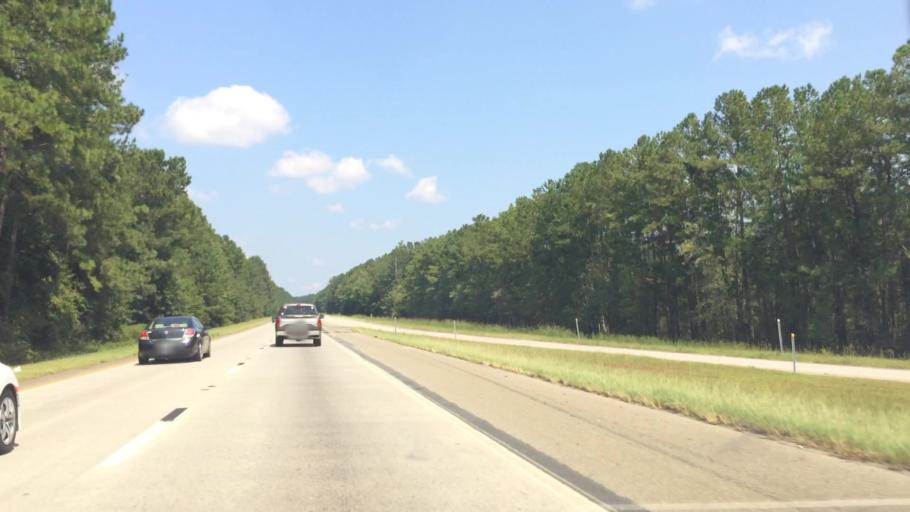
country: US
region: South Carolina
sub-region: Colleton County
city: Walterboro
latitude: 33.0058
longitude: -80.6683
